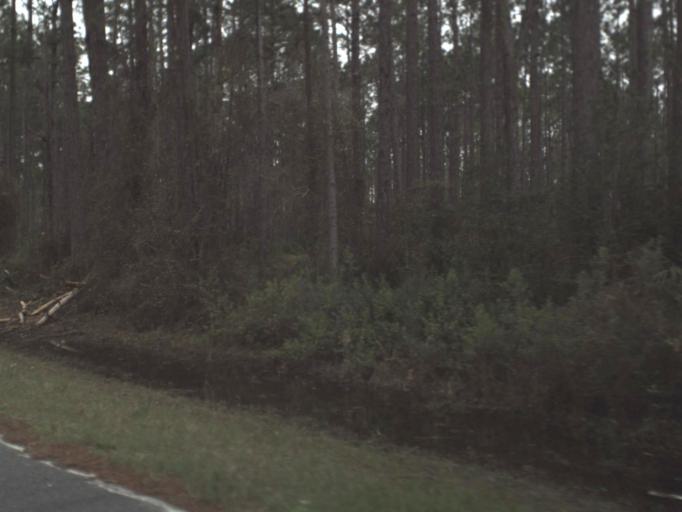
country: US
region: Florida
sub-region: Franklin County
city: Apalachicola
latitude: 29.9249
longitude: -84.9772
